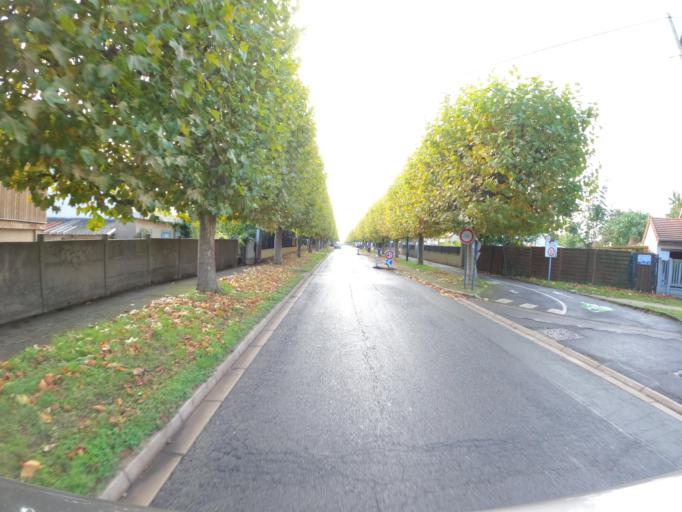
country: FR
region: Ile-de-France
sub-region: Departement de Seine-et-Marne
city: Brou-sur-Chantereine
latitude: 48.8924
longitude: 2.6178
